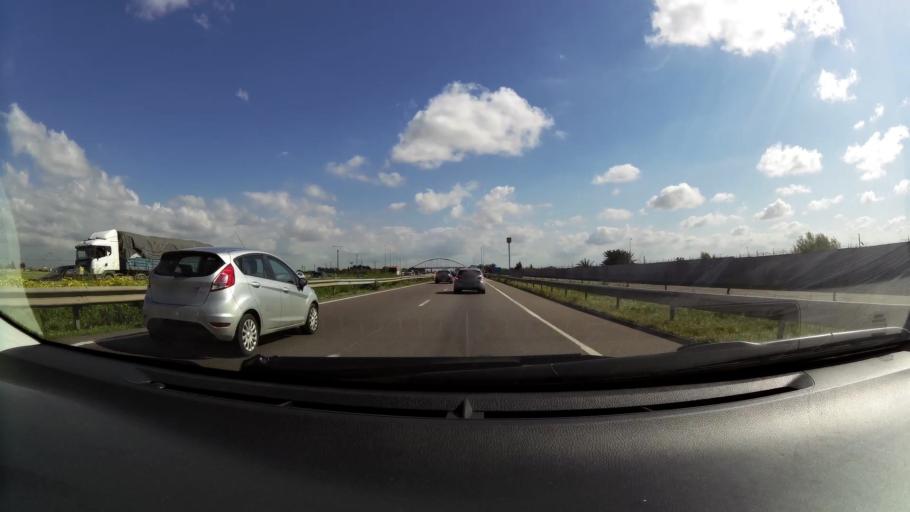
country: MA
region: Chaouia-Ouardigha
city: Nouaseur
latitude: 33.3734
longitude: -7.6216
